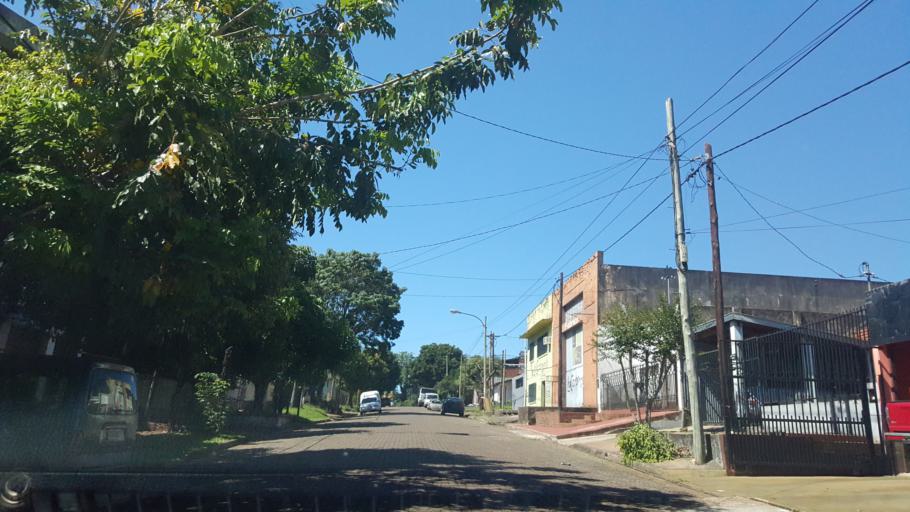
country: AR
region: Misiones
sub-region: Departamento de Capital
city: Posadas
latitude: -27.3891
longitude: -55.9030
